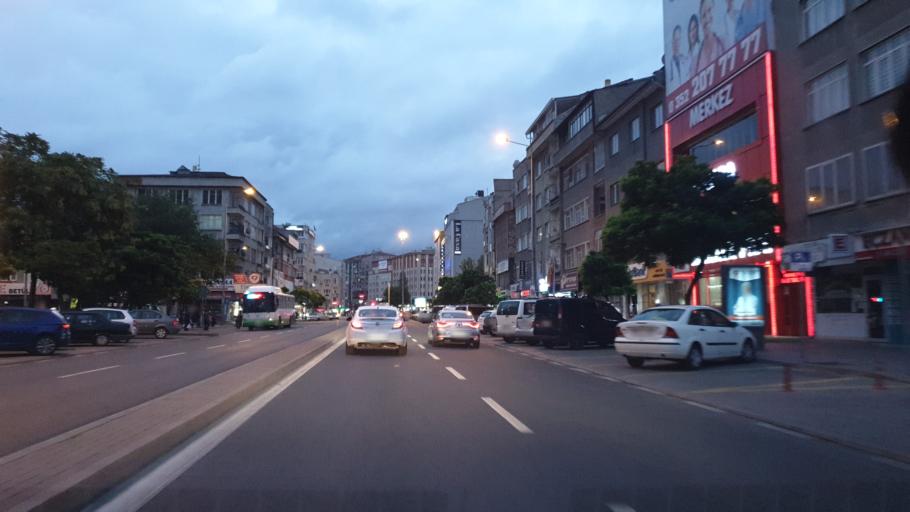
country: TR
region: Kayseri
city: Kayseri
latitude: 38.7224
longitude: 35.4819
